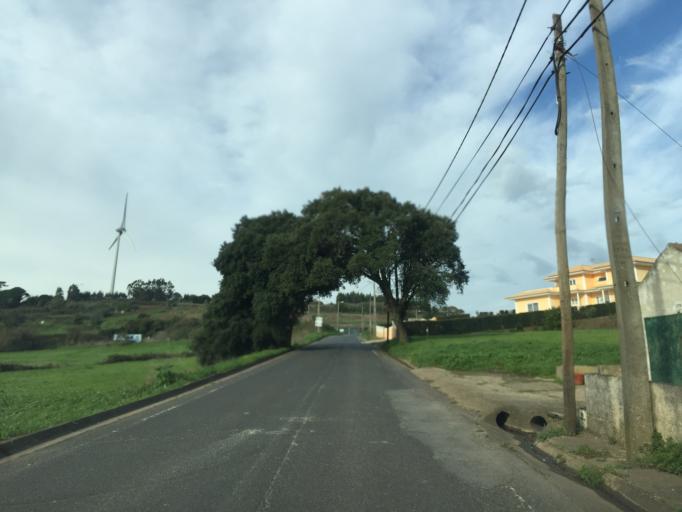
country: PT
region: Lisbon
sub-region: Sintra
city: Almargem
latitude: 38.8438
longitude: -9.2590
